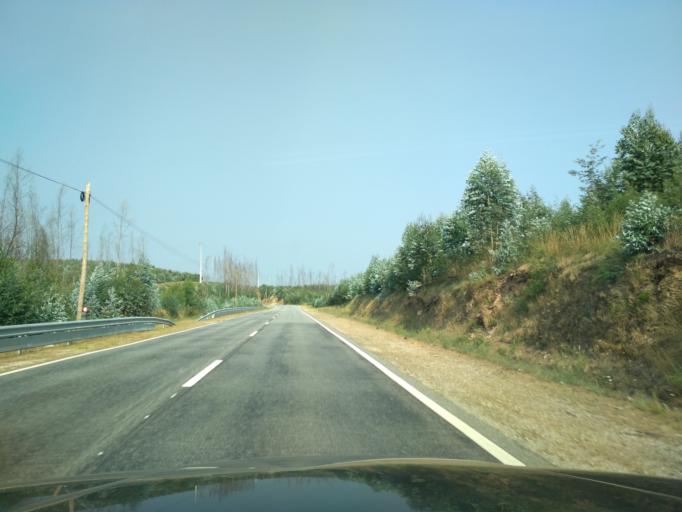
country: PT
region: Viseu
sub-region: Mortagua
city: Mortagua
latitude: 40.4038
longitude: -8.1975
